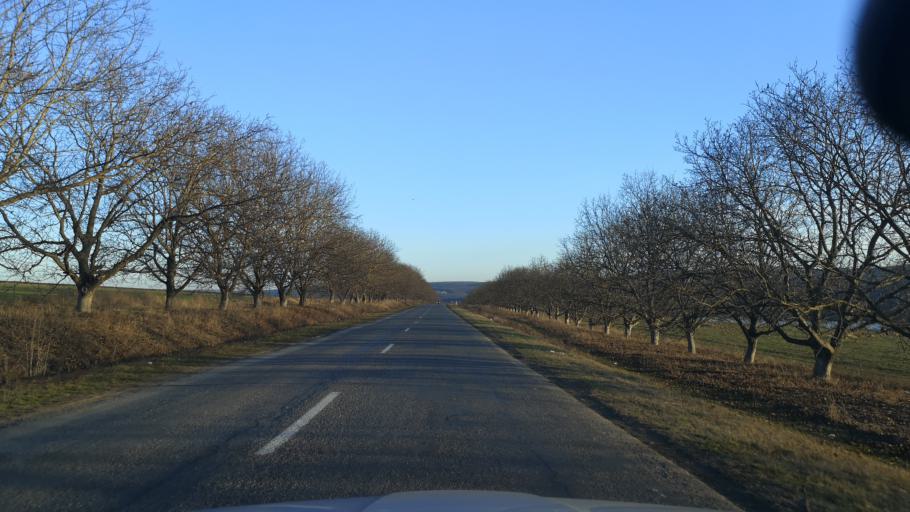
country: MD
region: Orhei
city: Orhei
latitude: 47.2895
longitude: 28.8167
